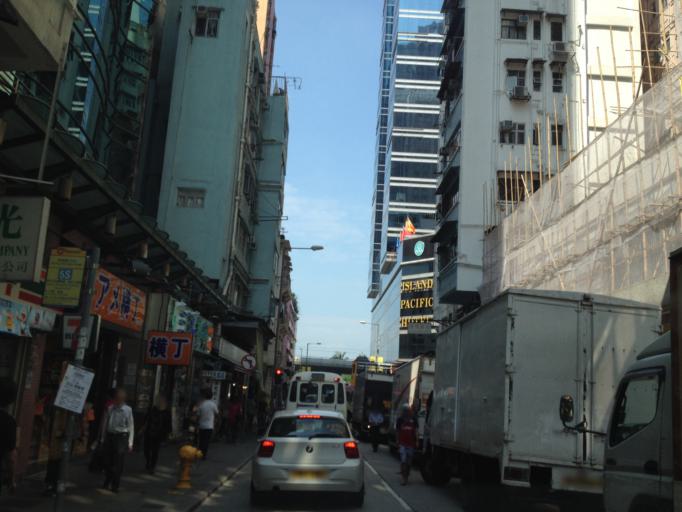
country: HK
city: Hong Kong
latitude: 22.2874
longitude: 114.1423
